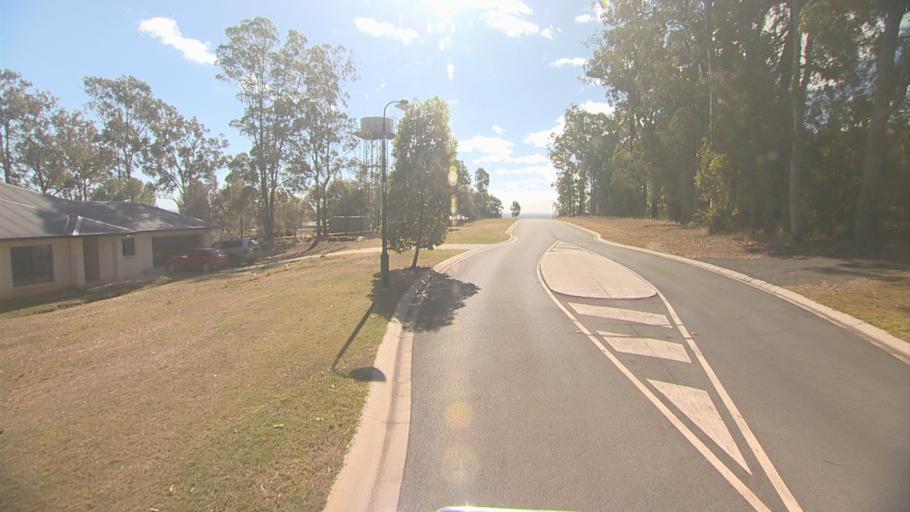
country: AU
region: Queensland
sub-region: Logan
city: Cedar Vale
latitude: -27.8935
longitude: 153.0019
